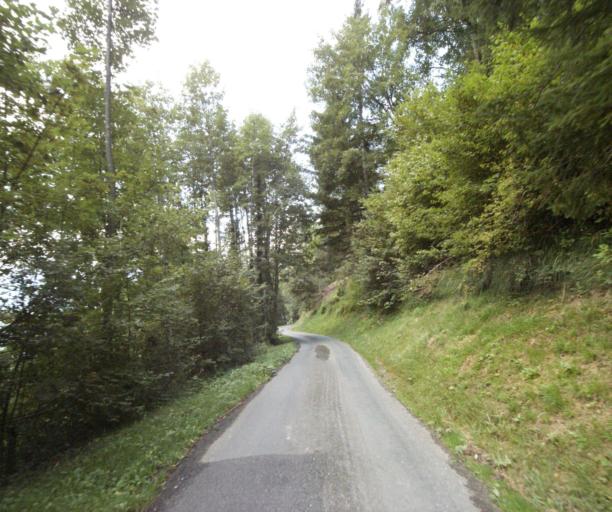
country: CH
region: Vaud
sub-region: Riviera-Pays-d'Enhaut District
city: Caux
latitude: 46.4147
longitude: 6.9626
